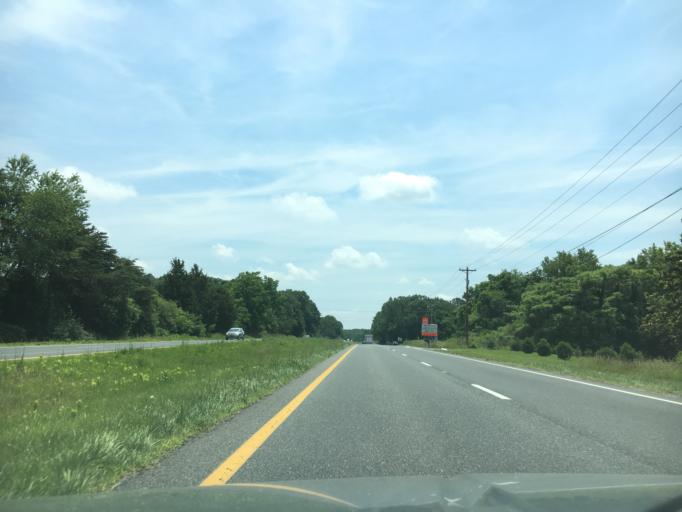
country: US
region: Virginia
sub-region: Campbell County
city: Concord
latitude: 37.3586
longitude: -79.0029
